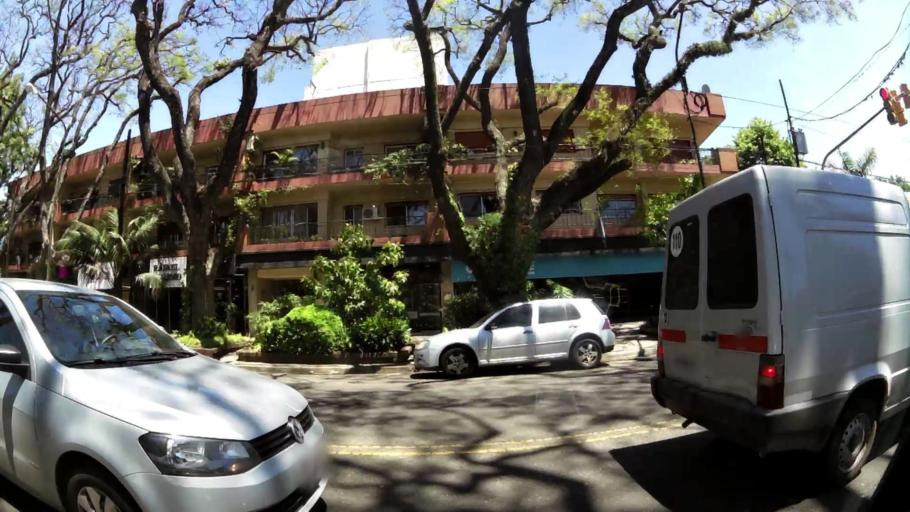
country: AR
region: Buenos Aires
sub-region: Partido de San Isidro
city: San Isidro
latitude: -34.4827
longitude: -58.4903
